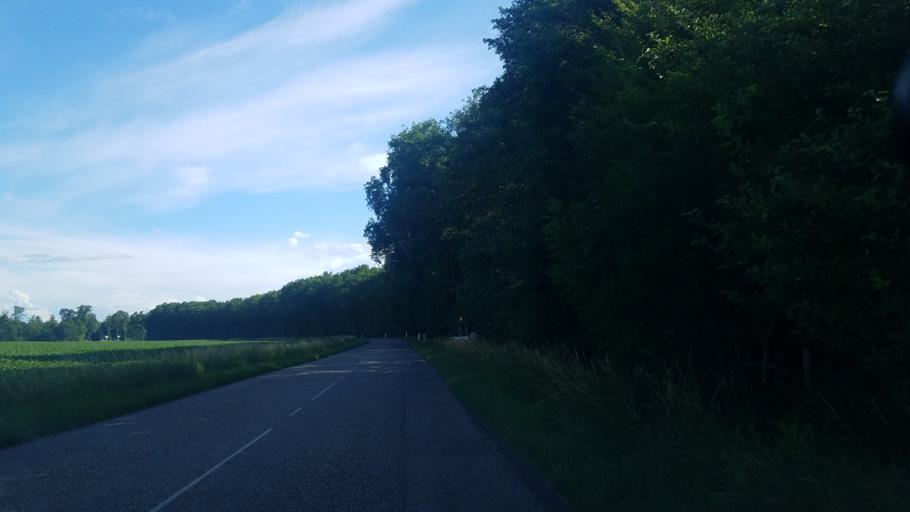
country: FR
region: Alsace
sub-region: Departement du Bas-Rhin
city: Soufflenheim
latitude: 48.8031
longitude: 7.9546
